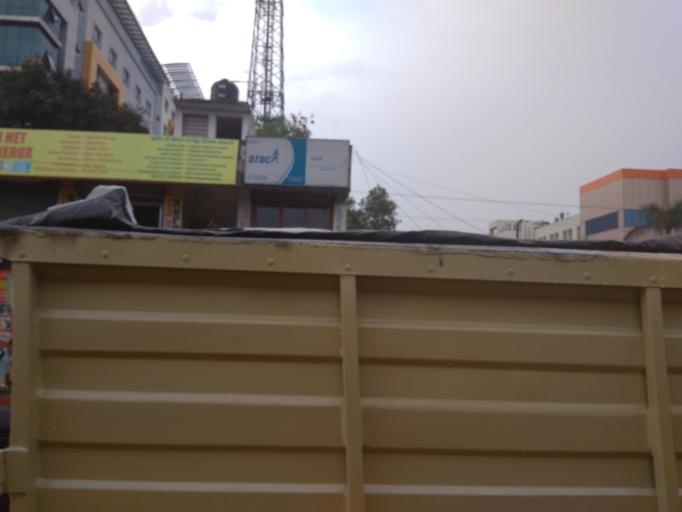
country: IN
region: Tamil Nadu
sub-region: Kancheepuram
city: Injambakkam
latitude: 12.9017
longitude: 80.2278
